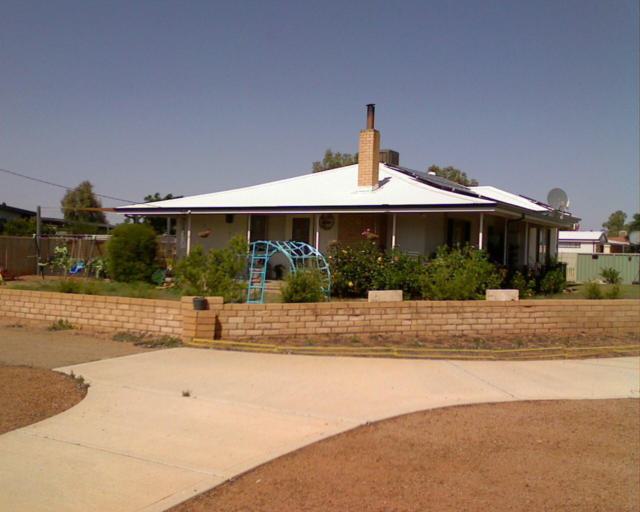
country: AU
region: Western Australia
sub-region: Merredin
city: Merredin
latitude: -30.9168
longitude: 118.2059
